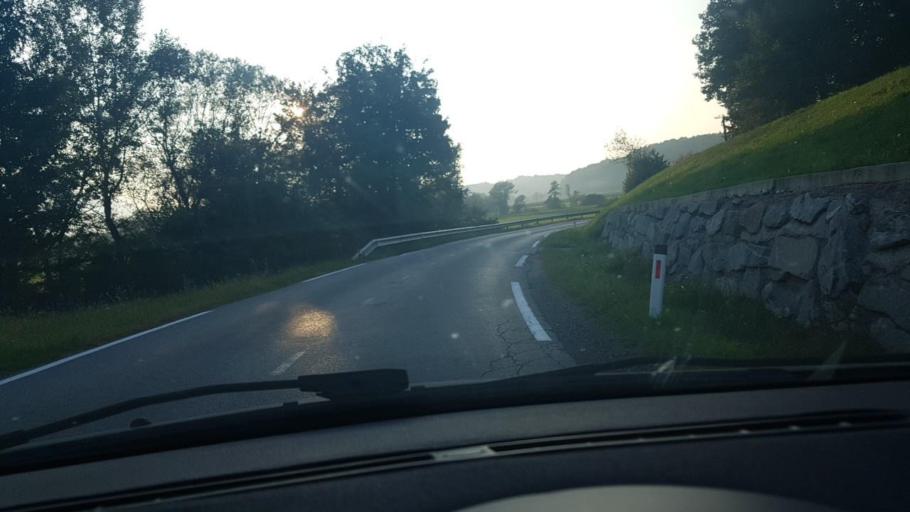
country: SI
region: Makole
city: Makole
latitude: 46.3334
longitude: 15.6964
